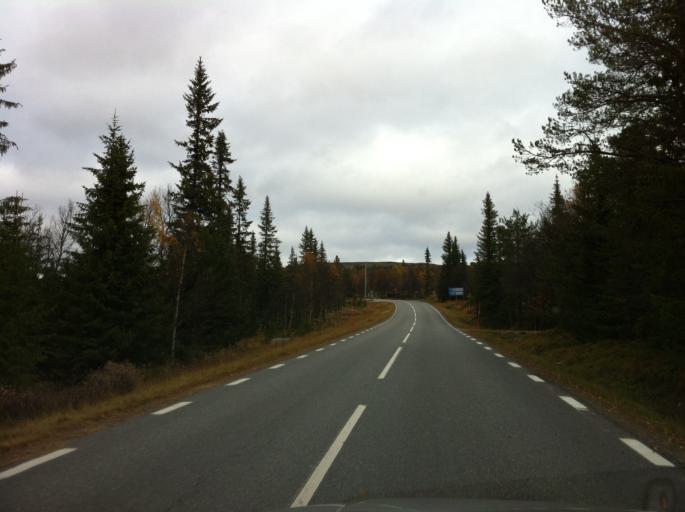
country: NO
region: Hedmark
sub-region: Engerdal
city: Engerdal
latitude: 62.0932
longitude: 12.3084
